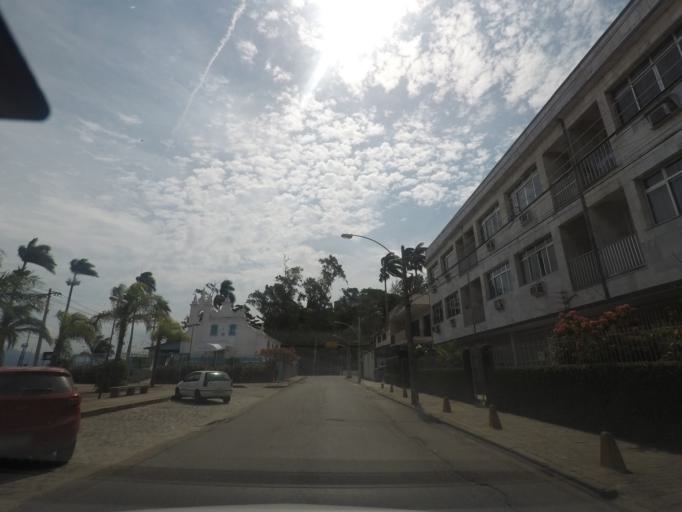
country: BR
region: Rio de Janeiro
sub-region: Rio De Janeiro
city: Rio de Janeiro
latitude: -22.8189
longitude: -43.2014
